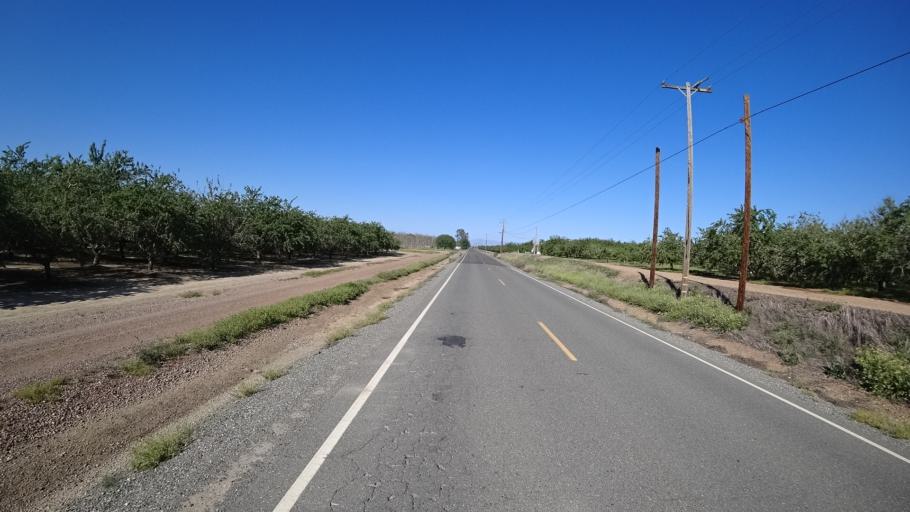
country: US
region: California
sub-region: Glenn County
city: Hamilton City
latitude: 39.7091
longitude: -122.0523
